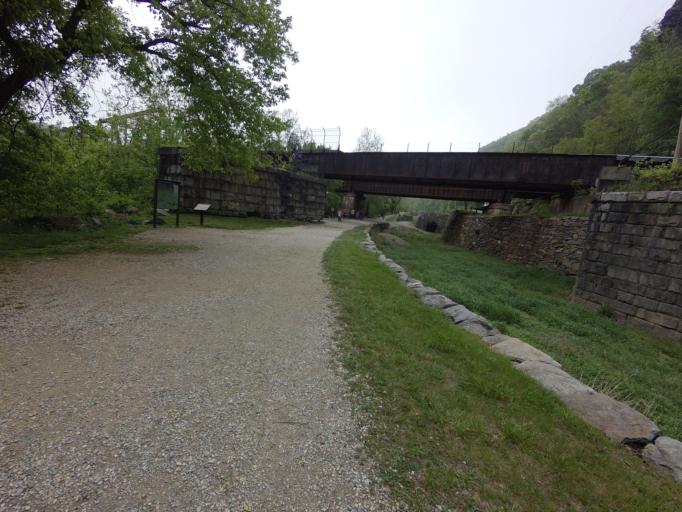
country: US
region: West Virginia
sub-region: Jefferson County
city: Bolivar
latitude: 39.3239
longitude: -77.7259
